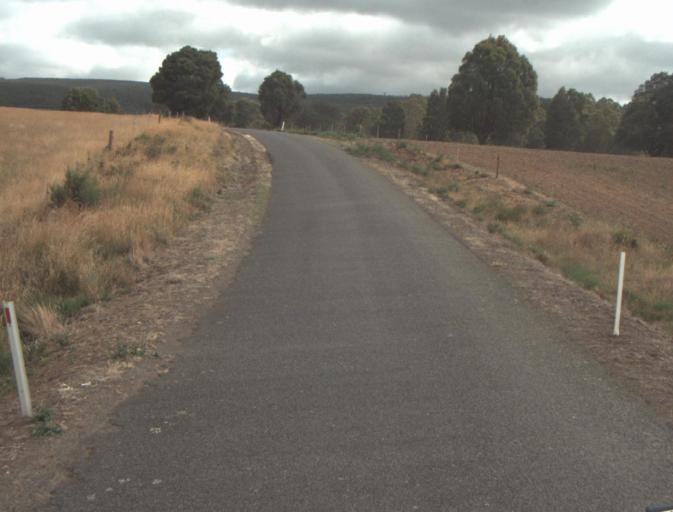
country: AU
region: Tasmania
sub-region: Northern Midlands
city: Evandale
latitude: -41.4729
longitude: 147.4971
